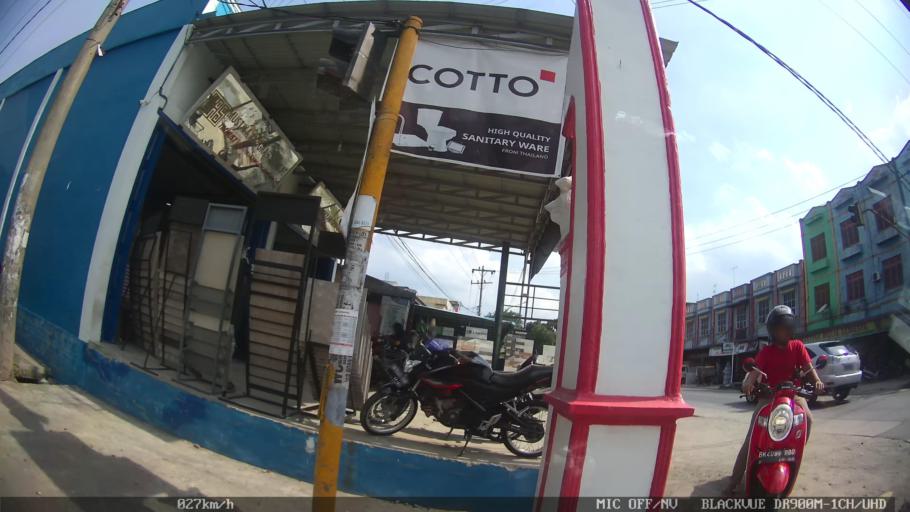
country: ID
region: North Sumatra
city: Binjai
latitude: 3.6438
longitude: 98.5104
